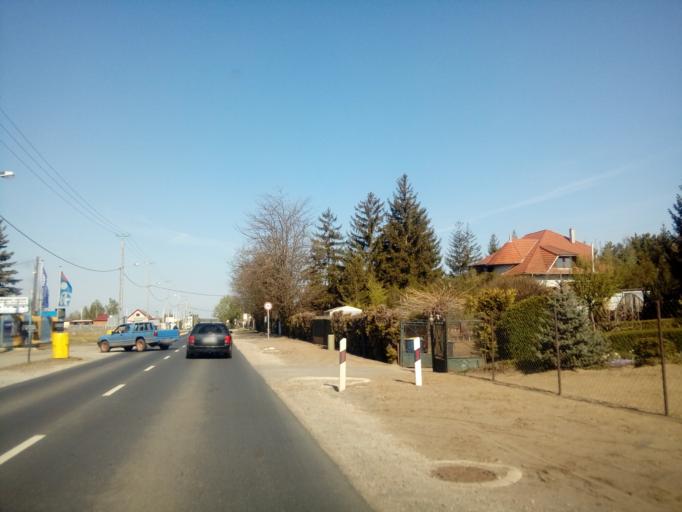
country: HU
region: Szabolcs-Szatmar-Bereg
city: Nagykallo
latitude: 47.8806
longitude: 21.8284
